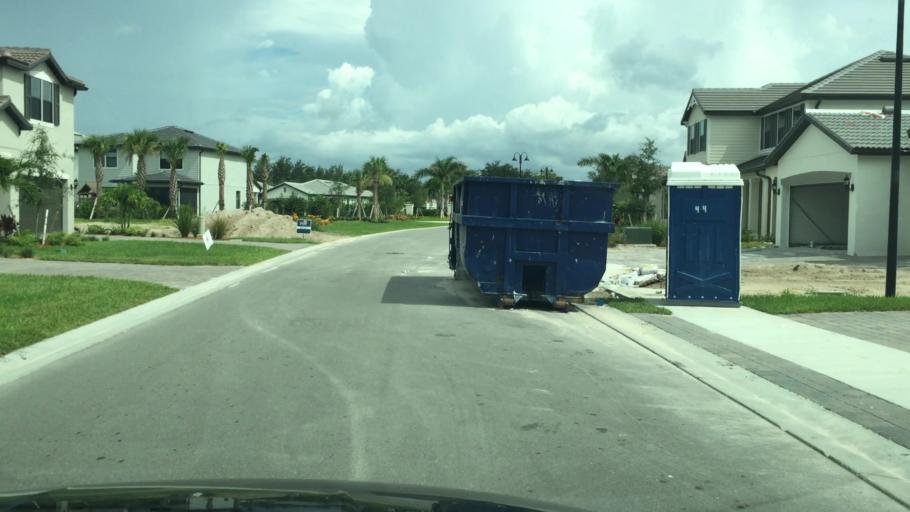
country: US
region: Florida
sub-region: Lee County
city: Three Oaks
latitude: 26.4869
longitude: -81.8026
